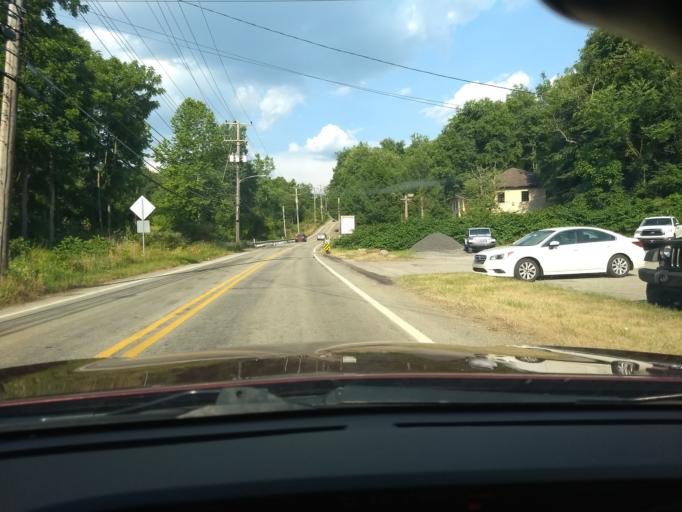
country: US
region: Pennsylvania
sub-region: Allegheny County
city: Plum
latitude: 40.4783
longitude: -79.7576
